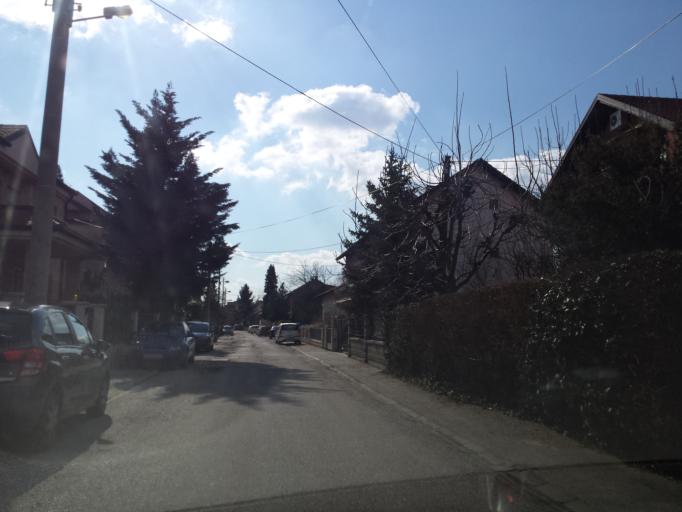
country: HR
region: Grad Zagreb
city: Stenjevec
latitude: 45.8112
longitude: 15.8950
